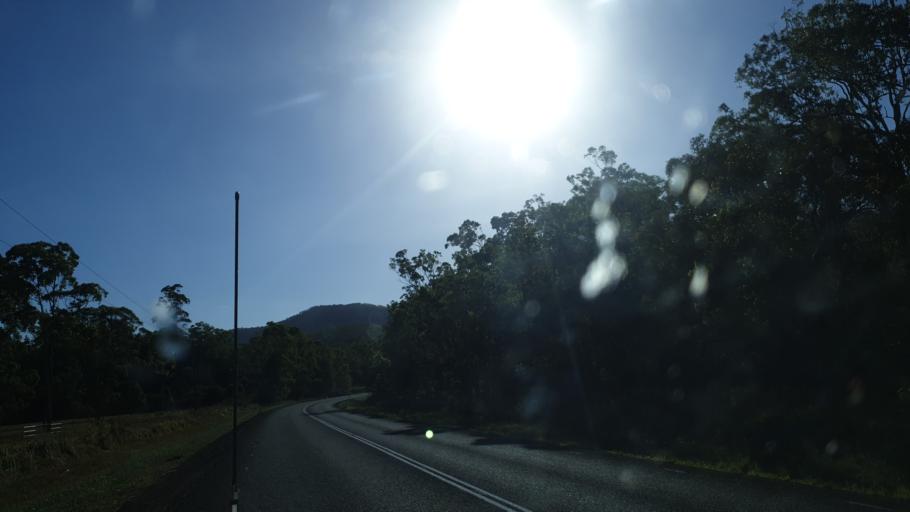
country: AU
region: Queensland
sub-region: Tablelands
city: Atherton
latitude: -17.3186
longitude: 145.4479
